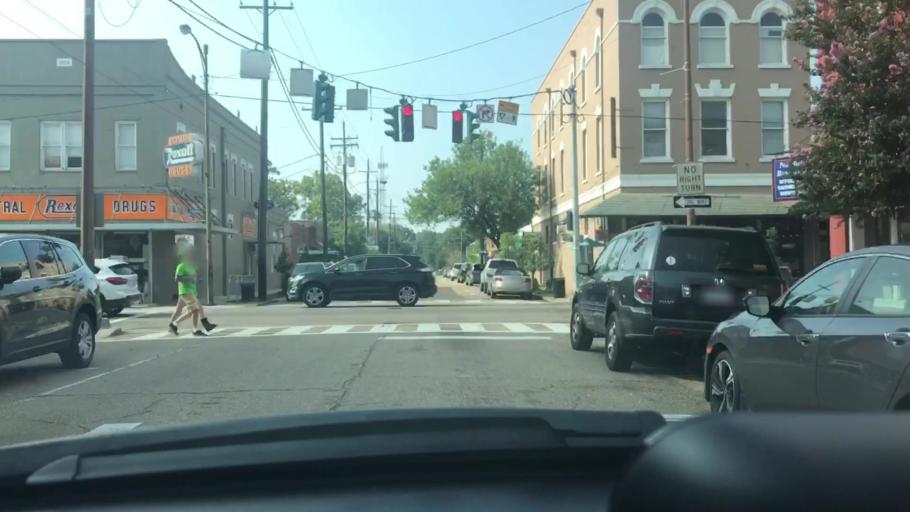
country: US
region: Louisiana
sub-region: Tangipahoa Parish
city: Hammond
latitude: 30.5042
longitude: -90.4596
